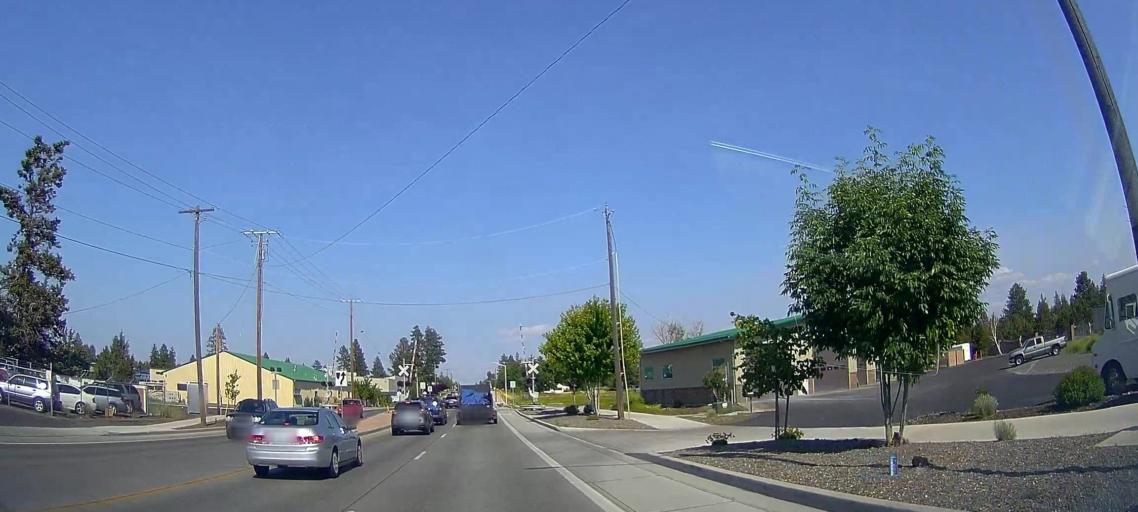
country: US
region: Oregon
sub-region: Deschutes County
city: Bend
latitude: 44.0370
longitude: -121.2898
